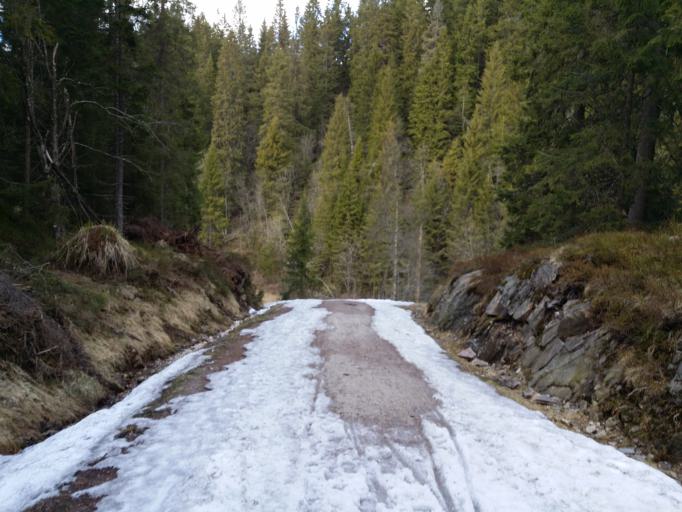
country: NO
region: Oslo
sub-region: Oslo
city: Sjolyststranda
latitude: 59.9881
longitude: 10.6879
